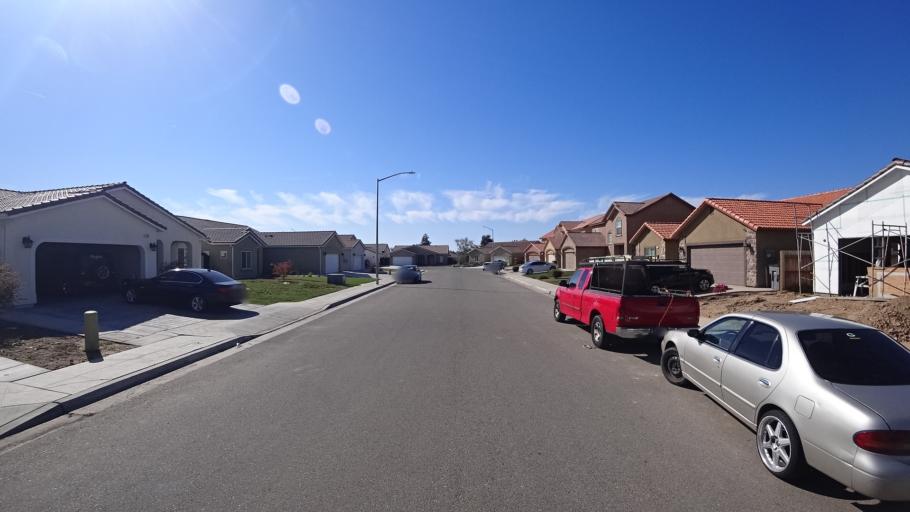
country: US
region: California
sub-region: Fresno County
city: West Park
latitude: 36.8037
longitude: -119.8872
